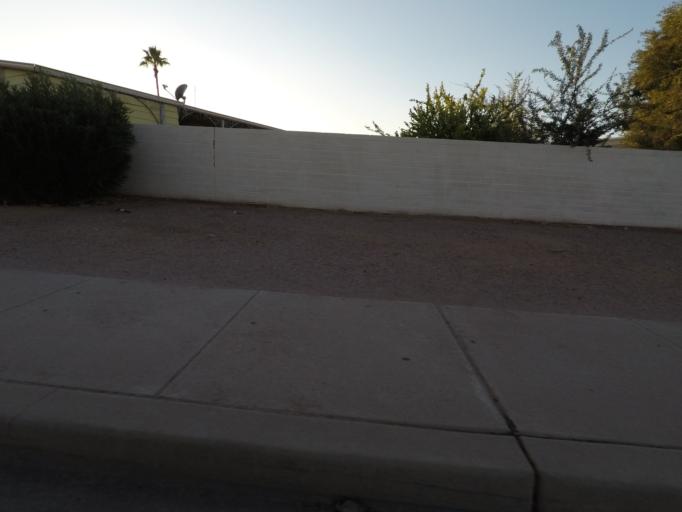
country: US
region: Arizona
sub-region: Maricopa County
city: Guadalupe
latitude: 33.3830
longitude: -111.9438
